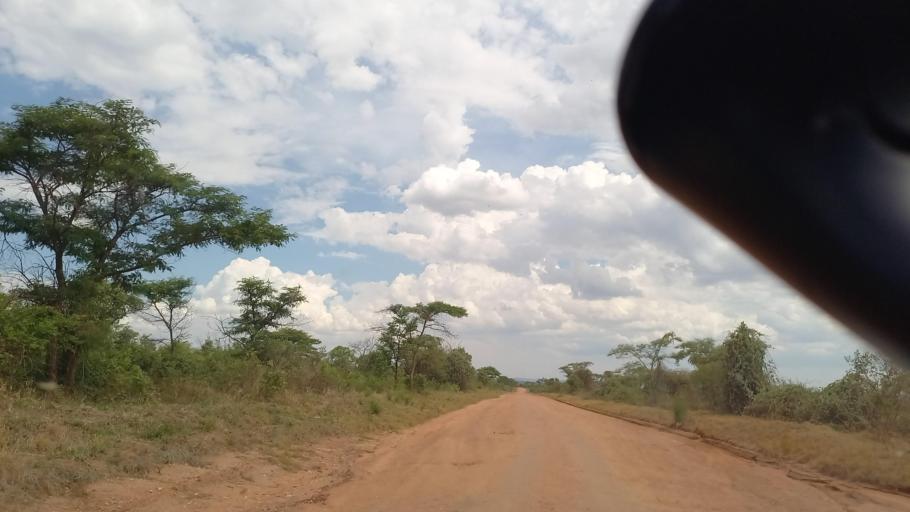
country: ZM
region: Southern
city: Nakambala
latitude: -16.0389
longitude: 27.9723
